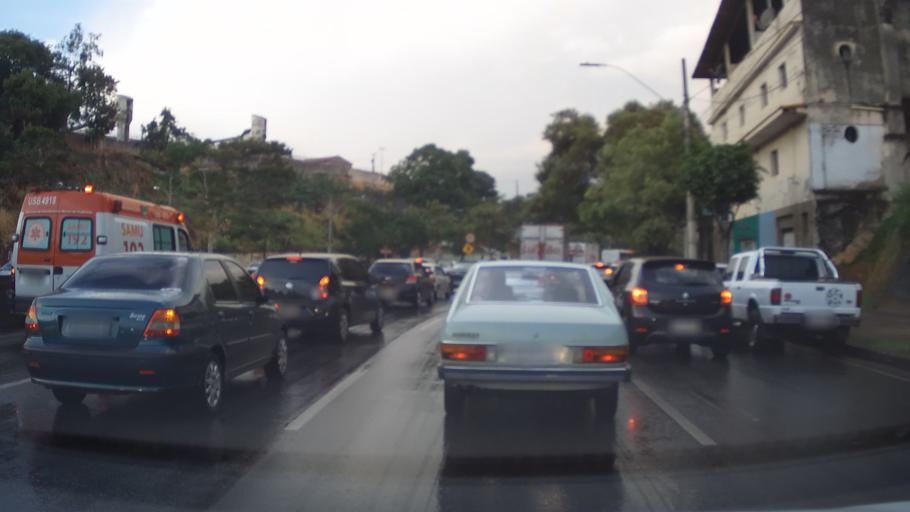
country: BR
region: Minas Gerais
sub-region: Belo Horizonte
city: Belo Horizonte
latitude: -19.9385
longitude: -43.9851
